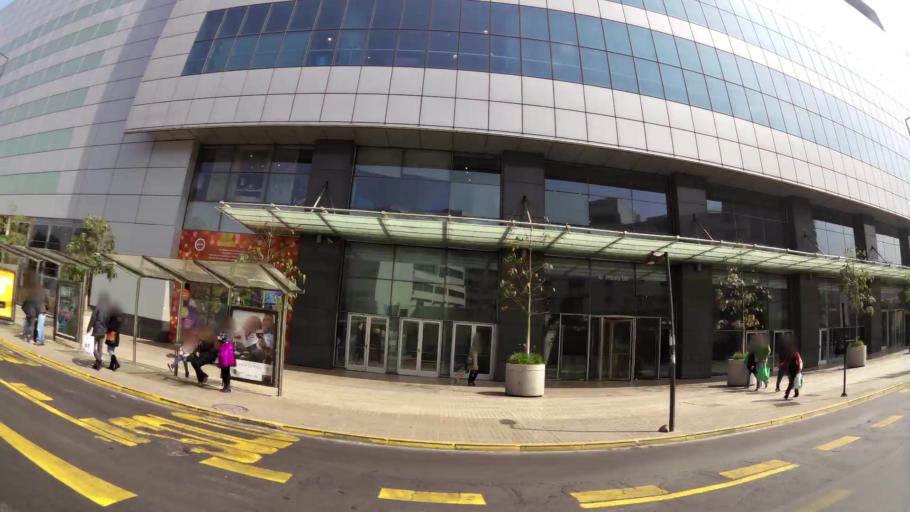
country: CL
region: Santiago Metropolitan
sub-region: Provincia de Santiago
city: Villa Presidente Frei, Nunoa, Santiago, Chile
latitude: -33.4184
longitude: -70.6055
